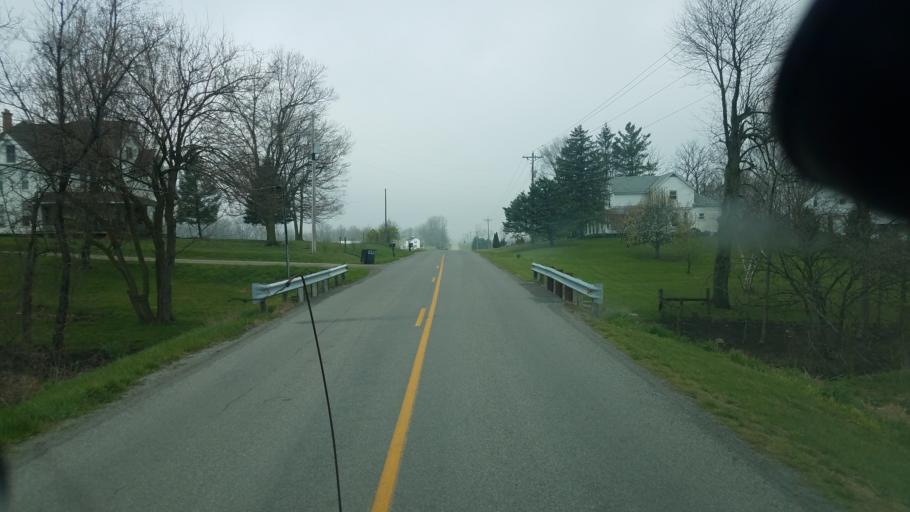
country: US
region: Ohio
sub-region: Logan County
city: Bellefontaine
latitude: 40.3855
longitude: -83.7947
